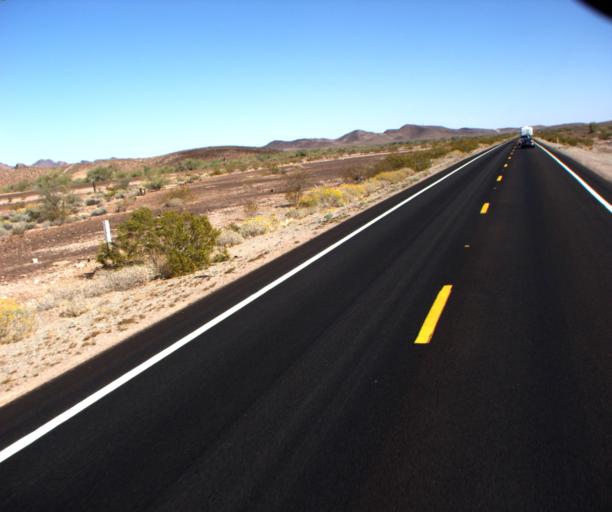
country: US
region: Arizona
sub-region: La Paz County
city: Quartzsite
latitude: 33.2002
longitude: -114.2687
